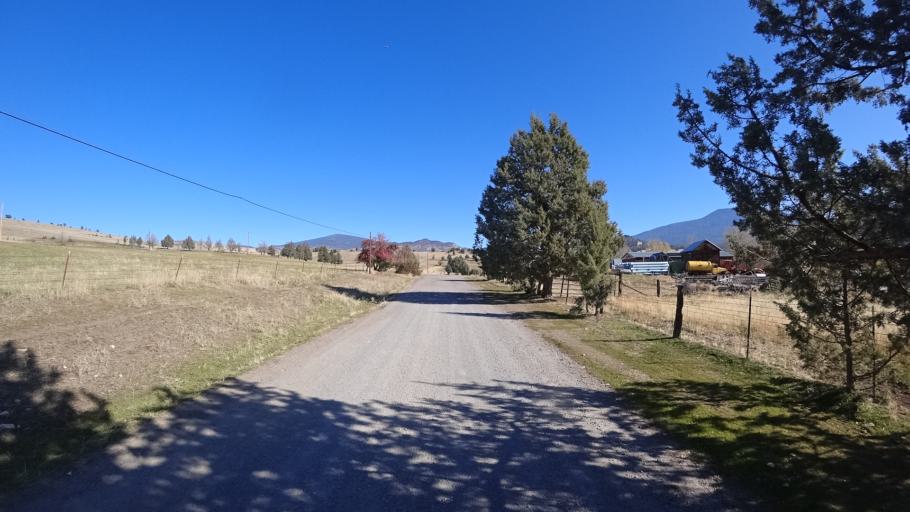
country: US
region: California
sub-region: Siskiyou County
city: Montague
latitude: 41.7391
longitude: -122.3413
